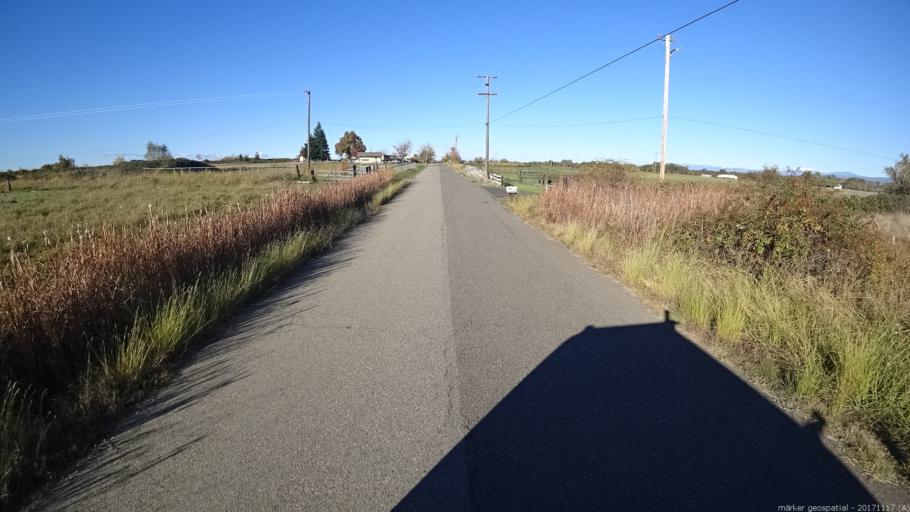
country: US
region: California
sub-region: Shasta County
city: Cottonwood
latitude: 40.3935
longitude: -122.2030
